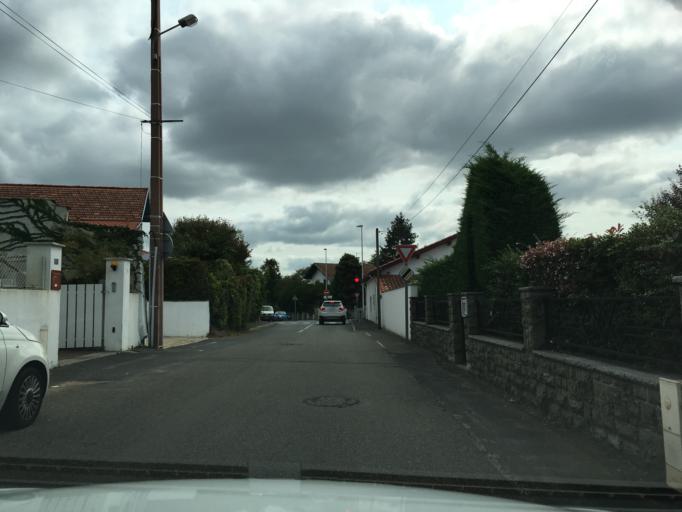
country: FR
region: Aquitaine
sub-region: Departement des Pyrenees-Atlantiques
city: Anglet
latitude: 43.4885
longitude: -1.5179
